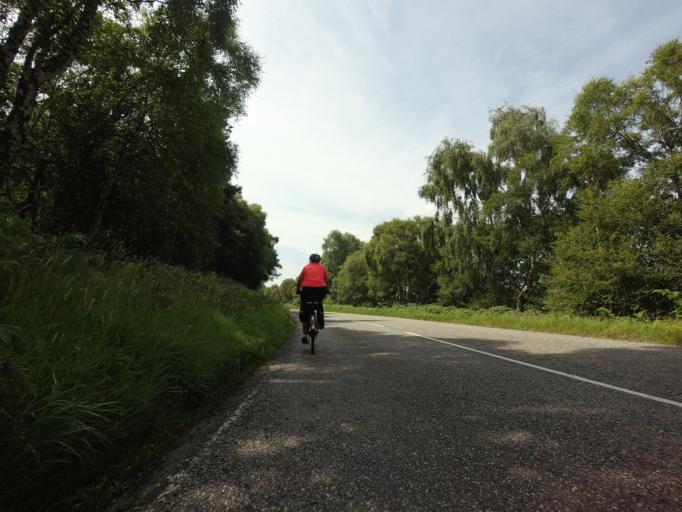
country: GB
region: Scotland
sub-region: Highland
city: Alness
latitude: 57.8581
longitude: -4.2383
